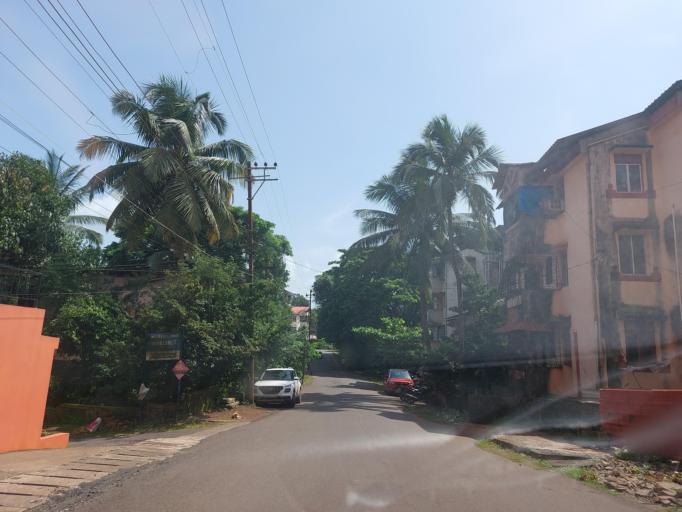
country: IN
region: Goa
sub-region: North Goa
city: Ponda
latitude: 15.3971
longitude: 74.0003
